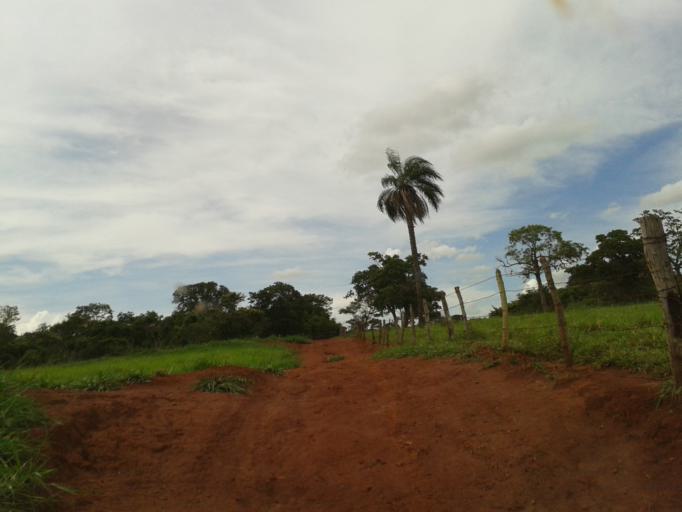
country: BR
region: Minas Gerais
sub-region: Santa Vitoria
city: Santa Vitoria
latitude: -18.7974
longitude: -49.8508
